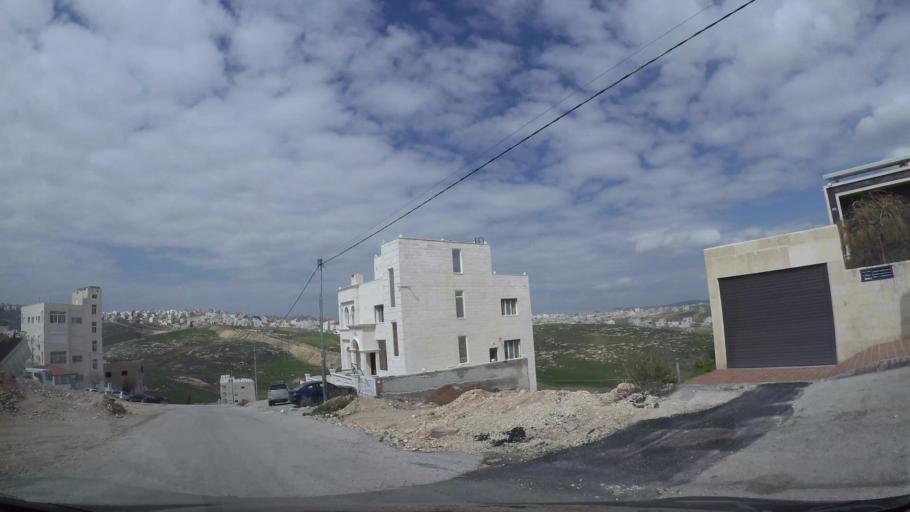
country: JO
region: Amman
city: Al Jubayhah
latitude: 32.0052
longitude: 35.9135
